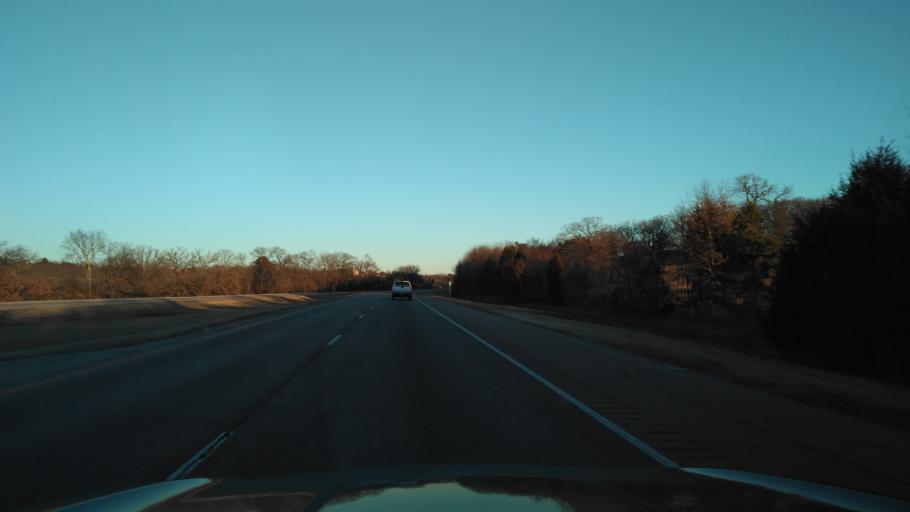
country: US
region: Arkansas
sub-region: Crawford County
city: Van Buren
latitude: 35.4628
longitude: -94.4116
